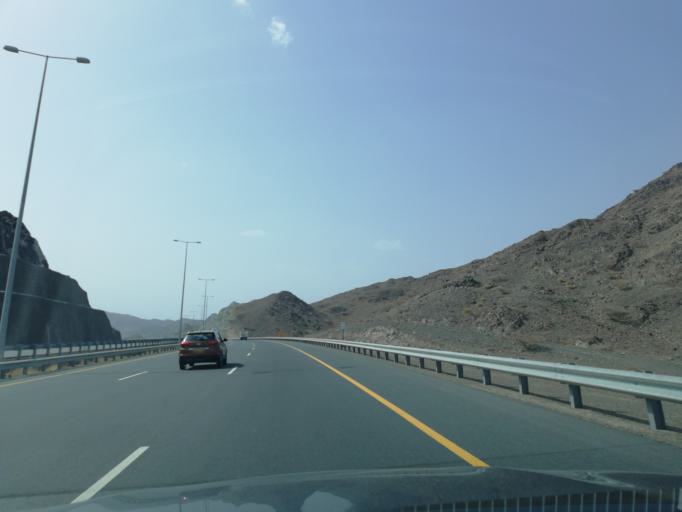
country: OM
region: Ash Sharqiyah
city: Ibra'
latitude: 22.9648
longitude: 58.2449
